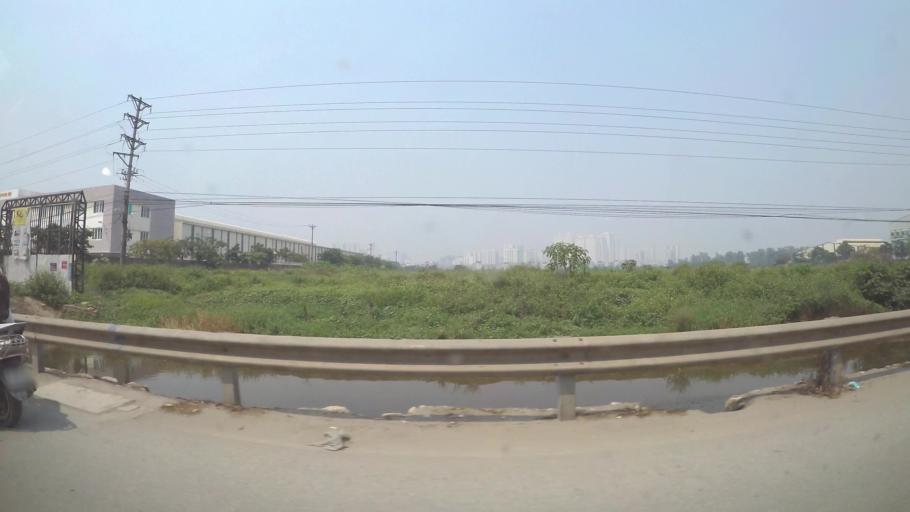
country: VN
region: Ha Noi
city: Van Dien
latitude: 20.9533
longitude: 105.8153
